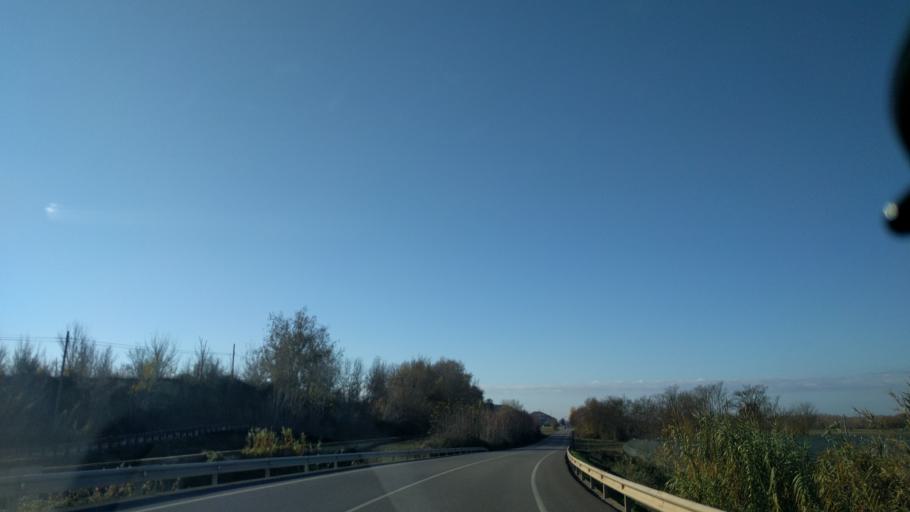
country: ES
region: Catalonia
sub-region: Provincia de Lleida
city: Corbins
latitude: 41.6738
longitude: 0.7130
